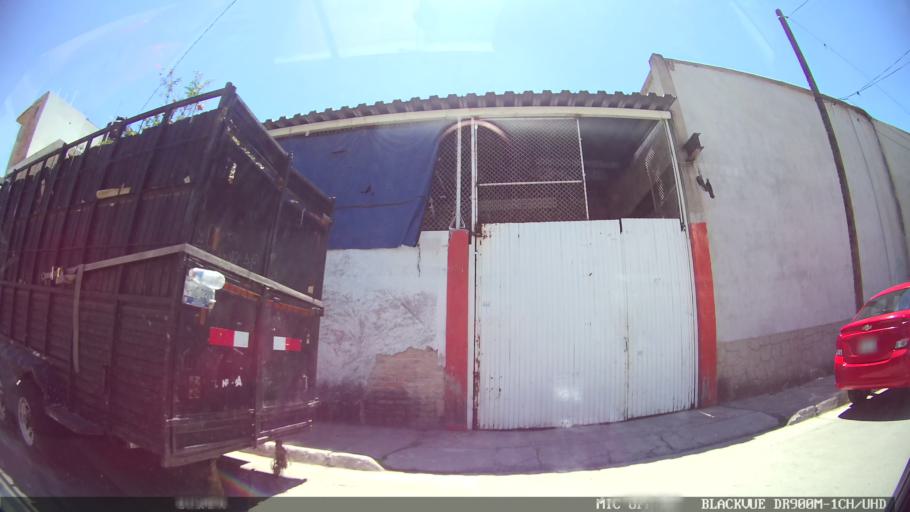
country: MX
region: Jalisco
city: Tlaquepaque
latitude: 20.6612
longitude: -103.2724
